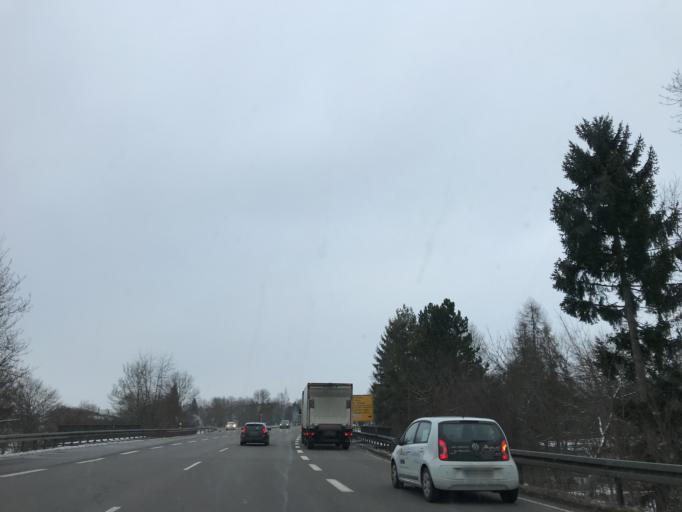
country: DE
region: Baden-Wuerttemberg
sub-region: Freiburg Region
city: Villingen-Schwenningen
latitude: 48.0572
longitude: 8.4709
